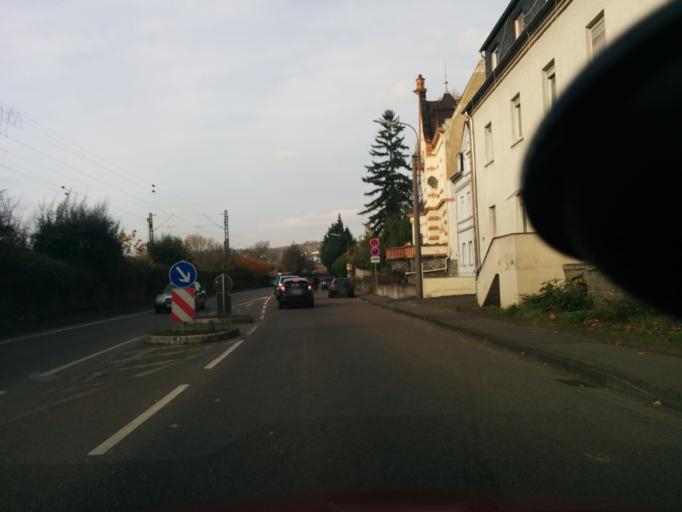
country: DE
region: Rheinland-Pfalz
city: Vallendar
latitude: 50.3909
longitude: 7.6177
